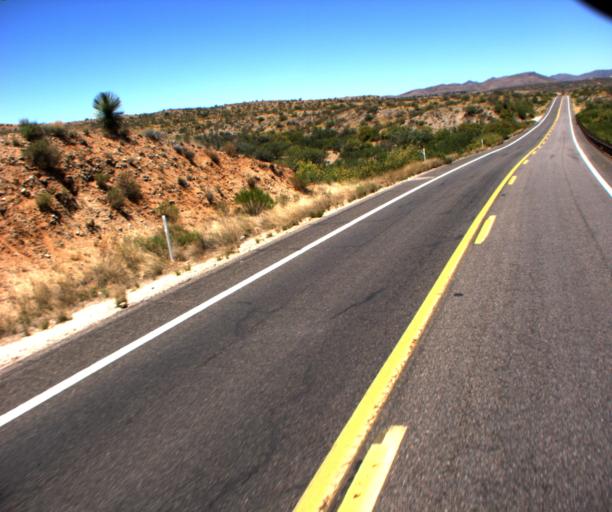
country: US
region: Arizona
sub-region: Gila County
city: Globe
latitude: 33.3521
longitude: -110.7340
